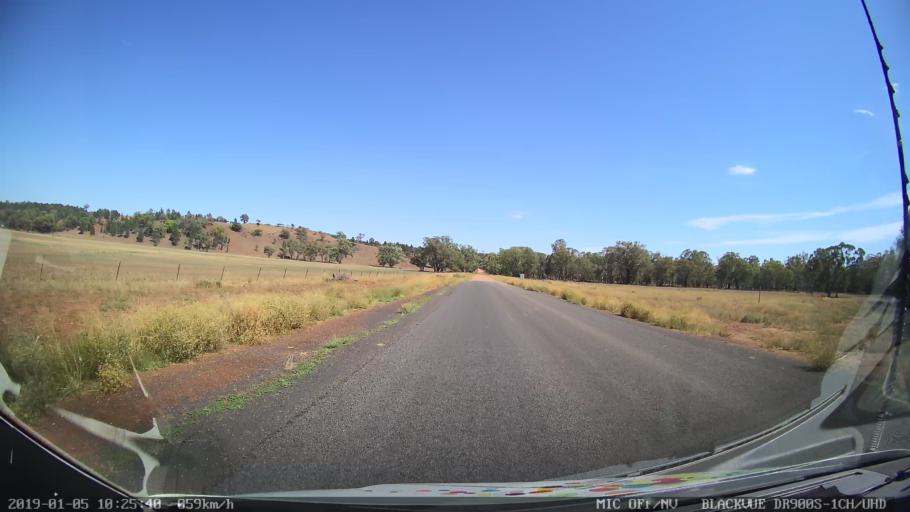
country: AU
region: New South Wales
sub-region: Gilgandra
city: Gilgandra
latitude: -31.5594
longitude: 148.9583
